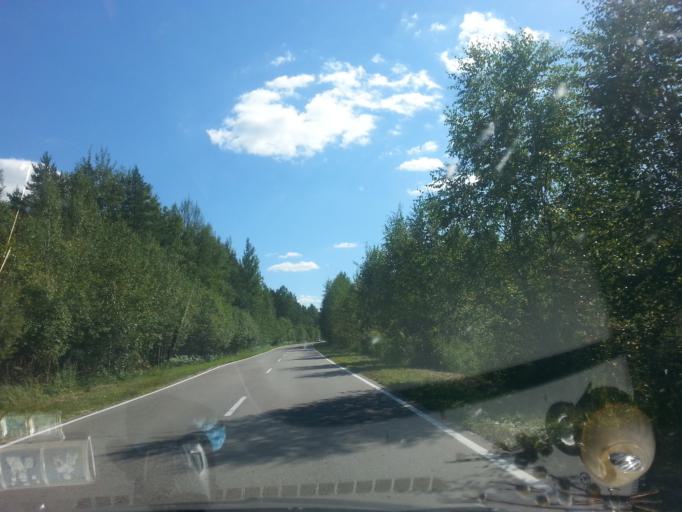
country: RU
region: Vladimir
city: Galitsy
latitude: 56.1341
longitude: 42.8738
